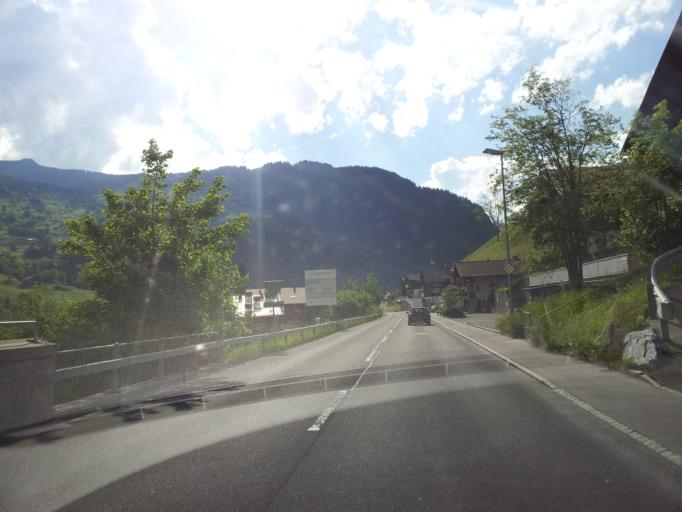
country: CH
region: Bern
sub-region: Interlaken-Oberhasli District
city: Grindelwald
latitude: 46.6259
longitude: 8.0190
